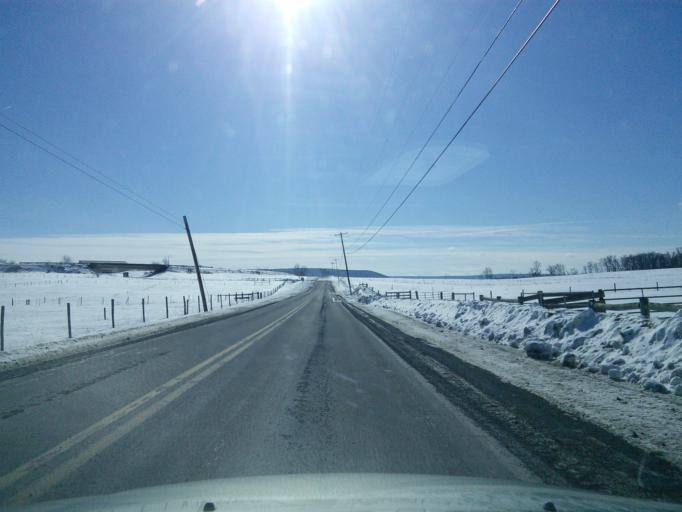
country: US
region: Pennsylvania
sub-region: Centre County
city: Houserville
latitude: 40.8661
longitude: -77.8402
